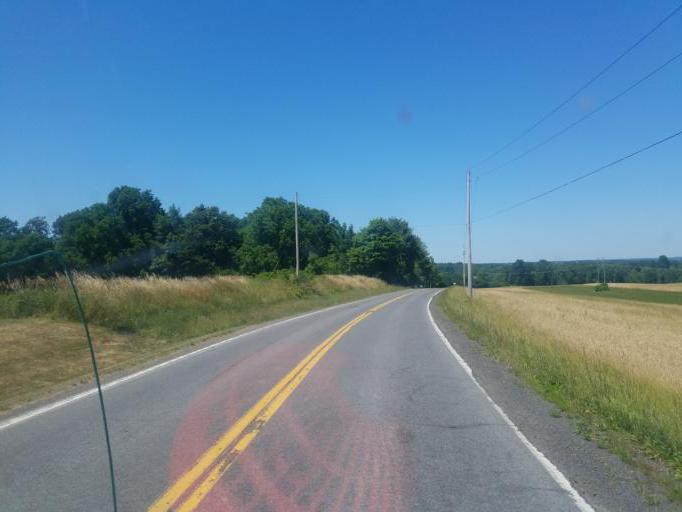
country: US
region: New York
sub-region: Yates County
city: Penn Yan
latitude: 42.7491
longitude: -77.0029
